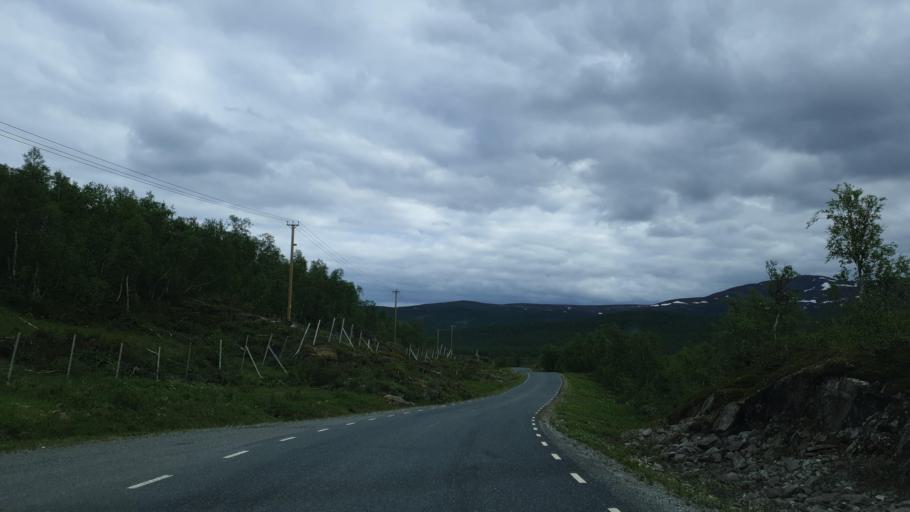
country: NO
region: Nordland
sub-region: Hattfjelldal
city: Hattfjelldal
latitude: 65.4185
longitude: 14.6823
